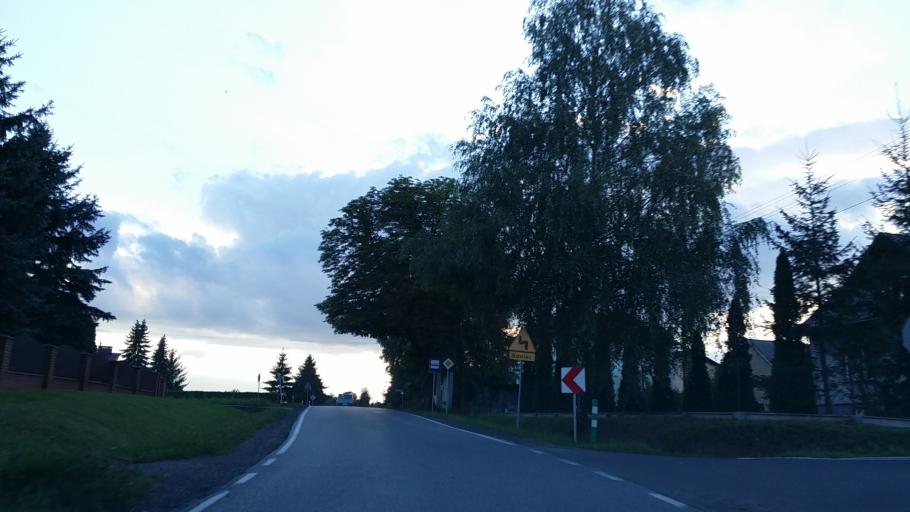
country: PL
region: Lesser Poland Voivodeship
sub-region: Powiat oswiecimski
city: Polanka Wielka
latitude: 49.9898
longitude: 19.3470
